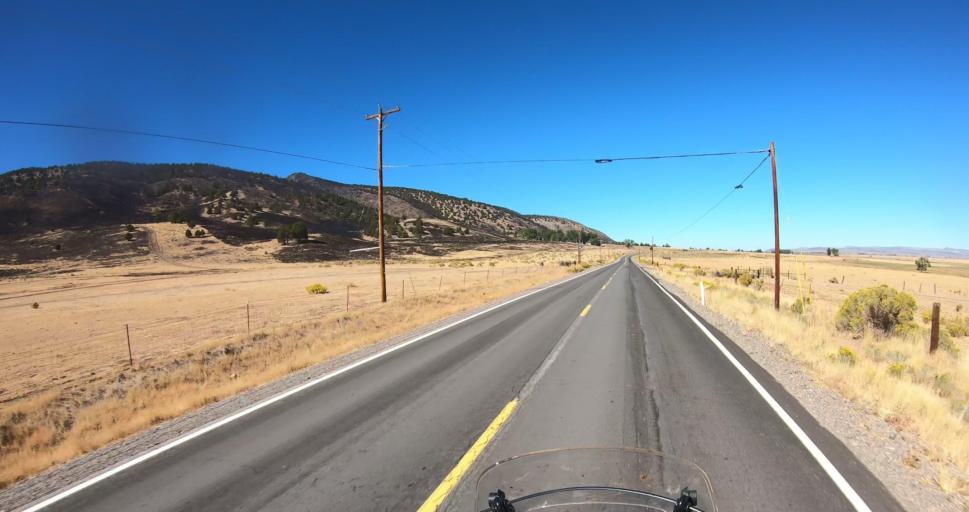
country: US
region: Oregon
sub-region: Lake County
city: Lakeview
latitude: 42.6348
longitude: -120.5170
